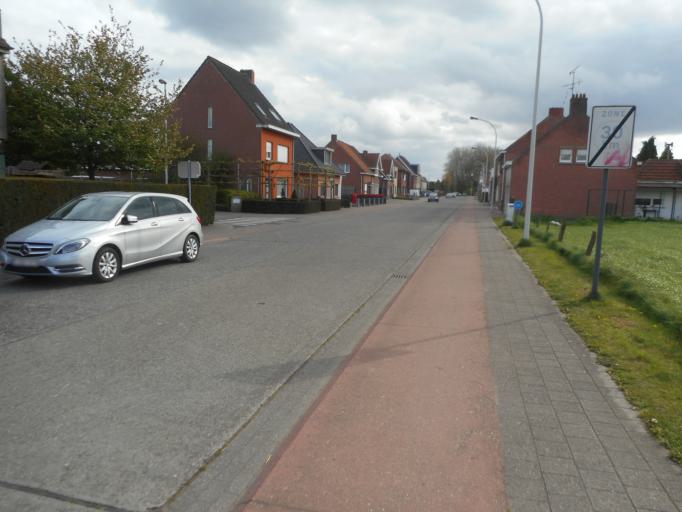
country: BE
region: Flanders
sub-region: Provincie Antwerpen
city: Wuustwezel
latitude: 51.3586
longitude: 4.5389
